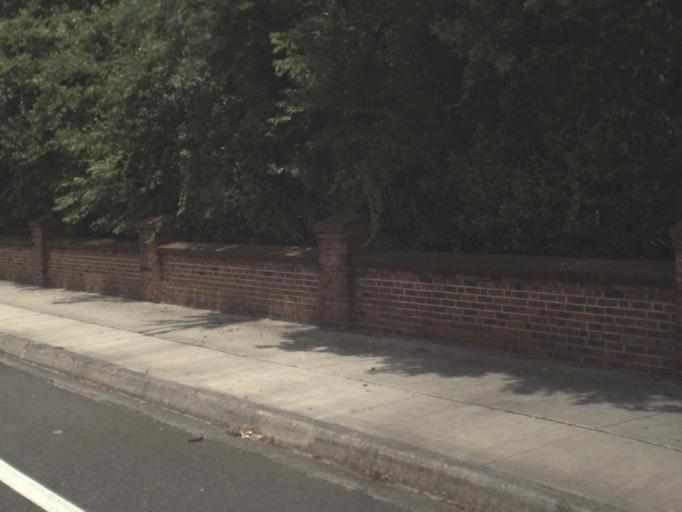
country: US
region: Florida
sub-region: Duval County
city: Jacksonville
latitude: 30.3664
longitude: -81.6526
